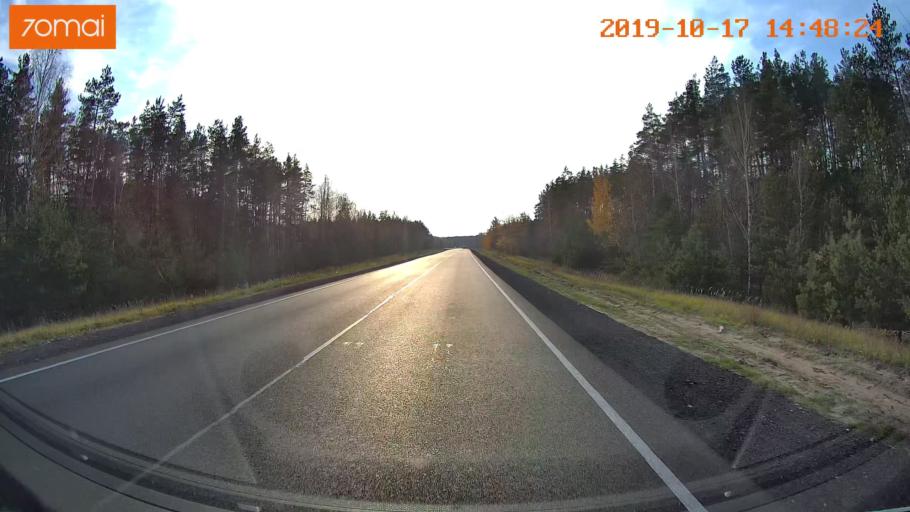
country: RU
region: Rjazan
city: Solotcha
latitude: 54.7595
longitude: 39.8468
